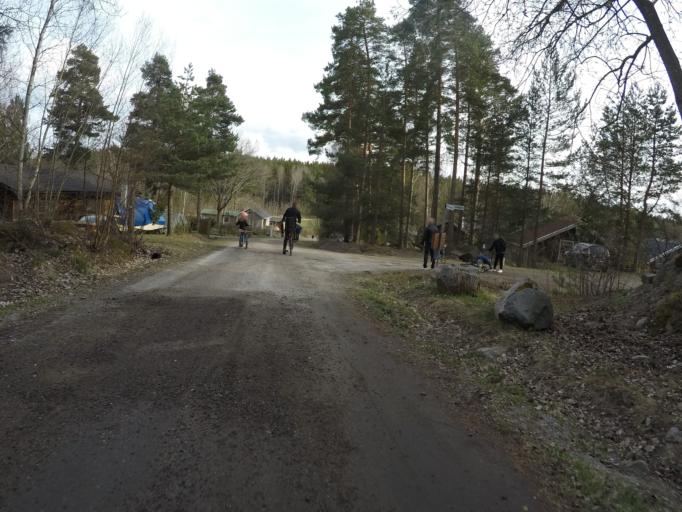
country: SE
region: Soedermanland
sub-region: Eskilstuna Kommun
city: Torshalla
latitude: 59.4292
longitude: 16.4960
